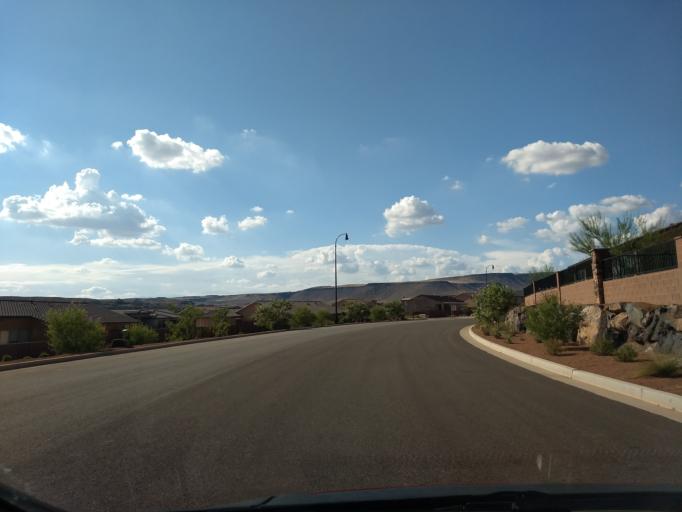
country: US
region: Utah
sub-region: Washington County
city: Washington
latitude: 37.1427
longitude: -113.5152
